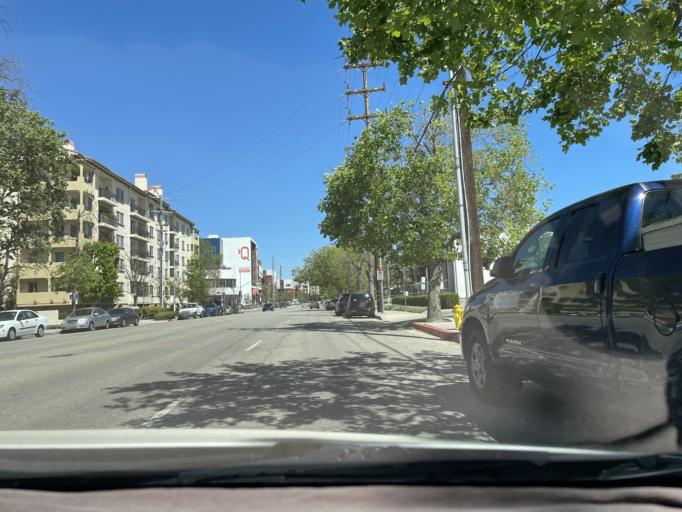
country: US
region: California
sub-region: Los Angeles County
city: Woodland Hills
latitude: 34.1828
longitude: -118.5943
